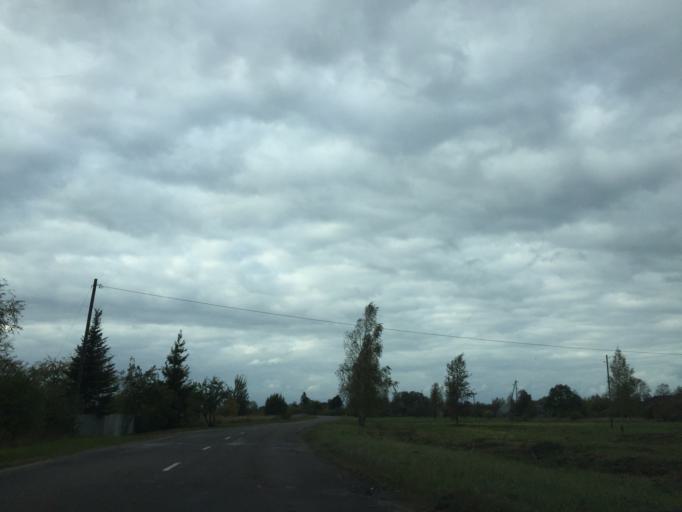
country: LV
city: Tireli
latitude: 56.8004
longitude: 23.6009
